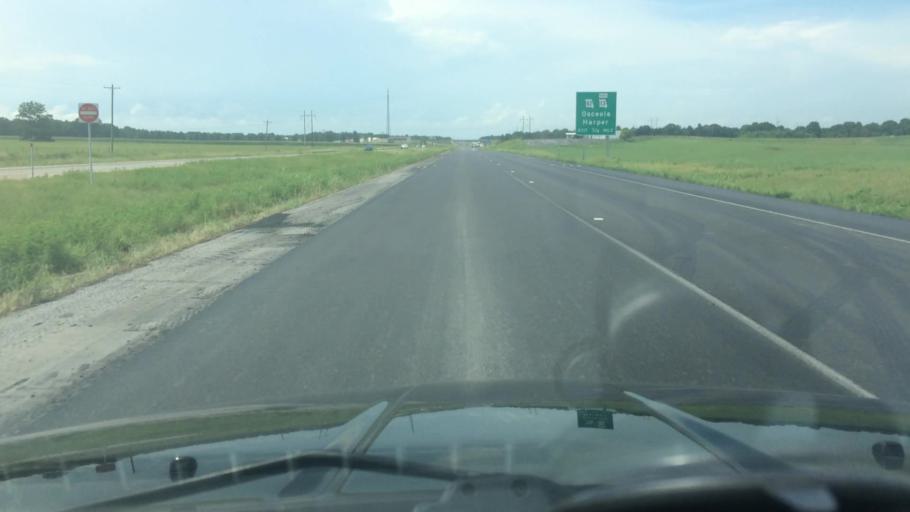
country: US
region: Missouri
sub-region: Saint Clair County
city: Osceola
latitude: 38.0277
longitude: -93.6743
